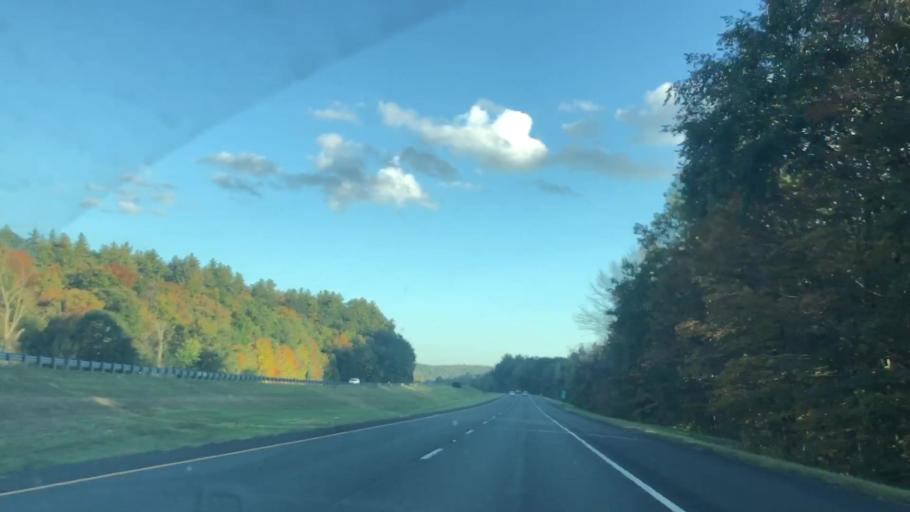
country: US
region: Massachusetts
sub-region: Franklin County
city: Bernardston
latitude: 42.7050
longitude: -72.5606
